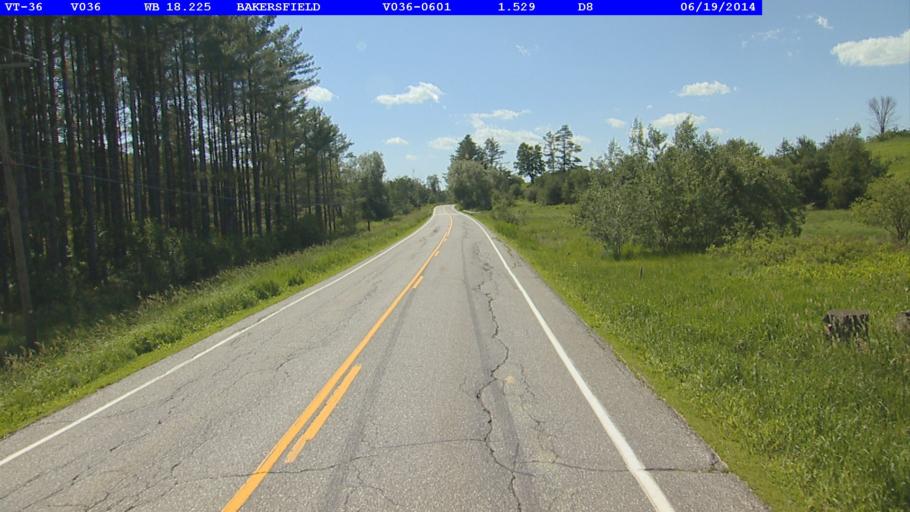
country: US
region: Vermont
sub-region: Franklin County
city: Enosburg Falls
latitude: 44.7814
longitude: -72.8204
